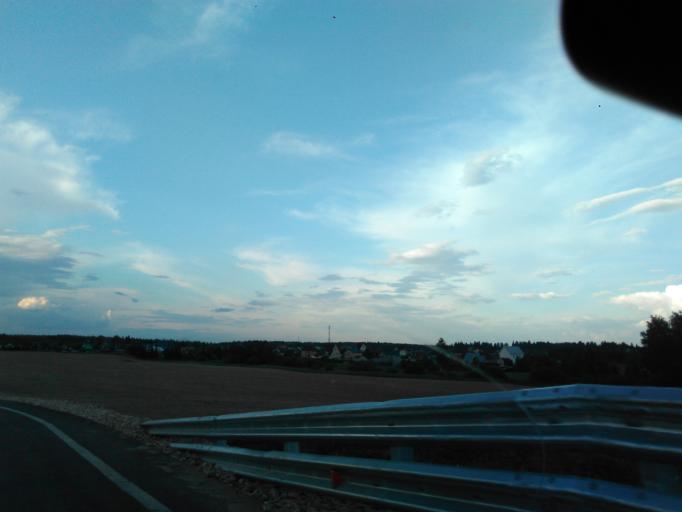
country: RU
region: Moskovskaya
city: Solnechnogorsk
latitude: 56.1420
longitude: 36.9783
